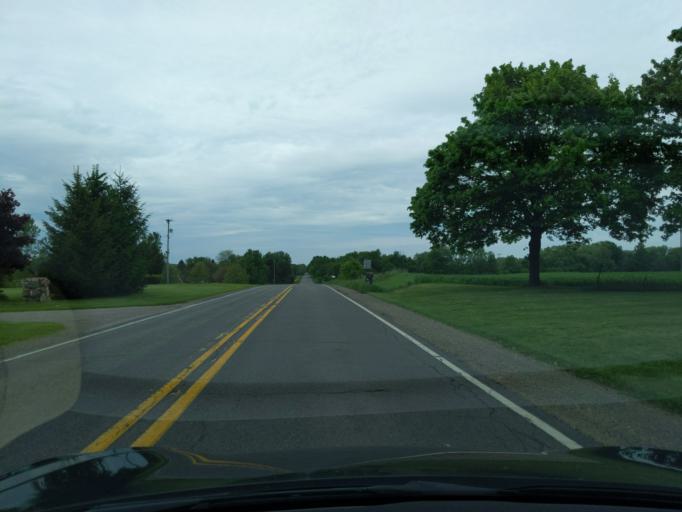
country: US
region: Michigan
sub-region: Ingham County
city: Leslie
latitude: 42.4935
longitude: -84.3562
